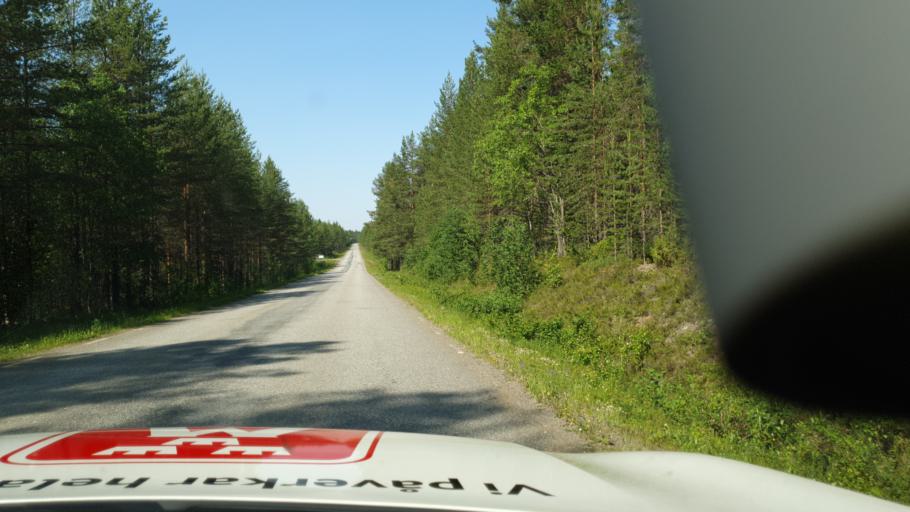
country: SE
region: Vaesterbotten
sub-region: Skelleftea Kommun
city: Langsele
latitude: 64.9434
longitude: 19.9574
